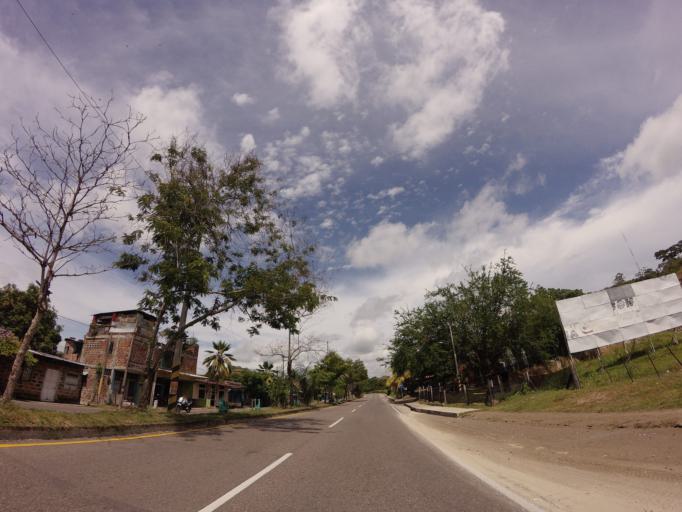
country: CO
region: Caldas
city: La Dorada
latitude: 5.4593
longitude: -74.6705
